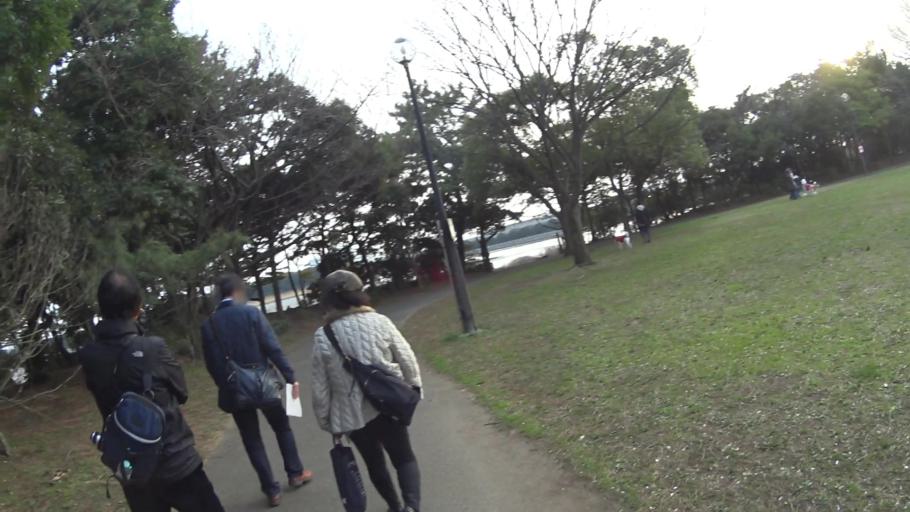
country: JP
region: Chiba
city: Funabashi
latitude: 35.6796
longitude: 140.0052
